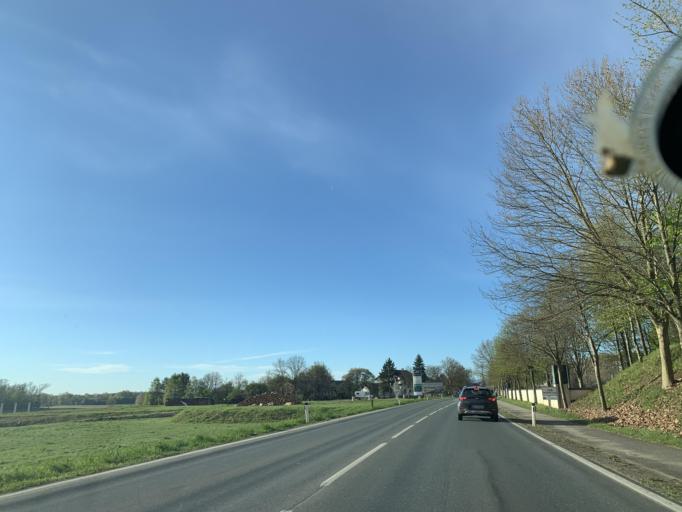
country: AT
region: Styria
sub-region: Politischer Bezirk Leibnitz
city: Lang
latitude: 46.8429
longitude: 15.5176
